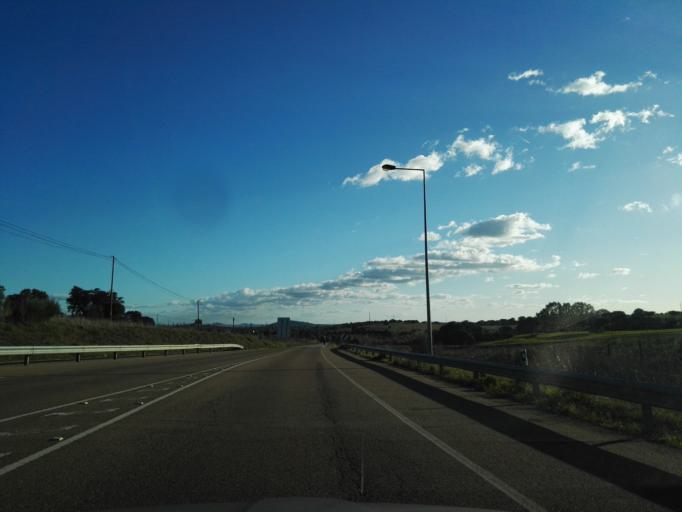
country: PT
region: Portalegre
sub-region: Elvas
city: Elvas
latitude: 38.9052
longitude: -7.1791
